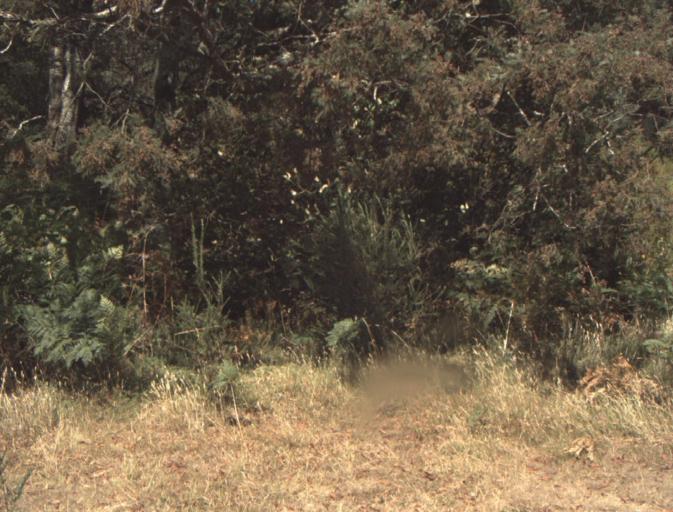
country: AU
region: Tasmania
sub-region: Launceston
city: Newstead
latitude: -41.3533
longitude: 147.3794
